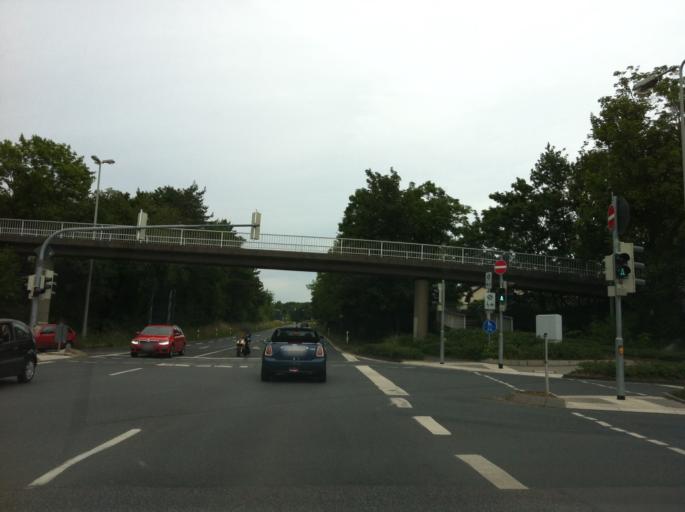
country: DE
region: Hesse
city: Sulzbach
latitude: 50.1381
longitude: 8.5178
